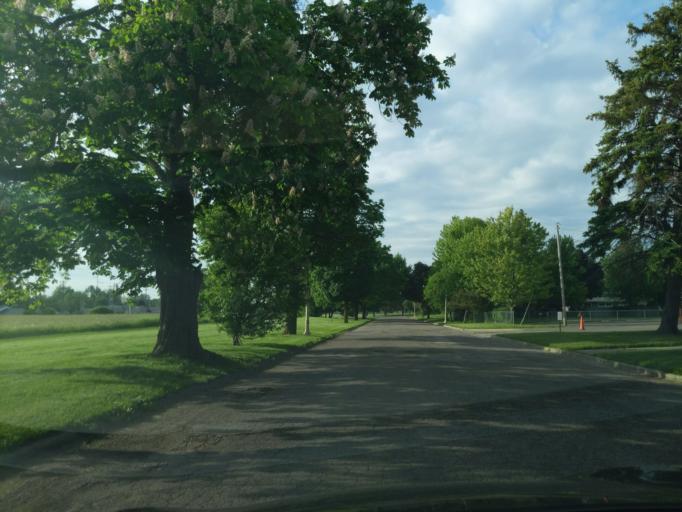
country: US
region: Michigan
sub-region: Ingham County
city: Edgemont Park
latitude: 42.7267
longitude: -84.5808
